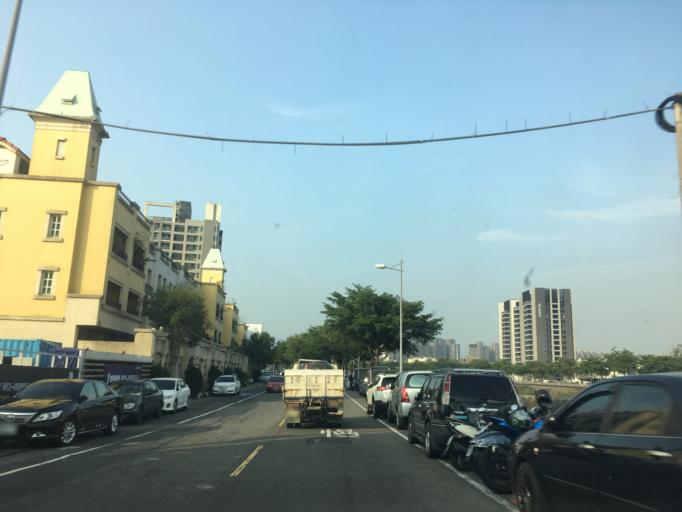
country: TW
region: Taiwan
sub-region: Taichung City
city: Taichung
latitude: 24.1540
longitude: 120.7021
